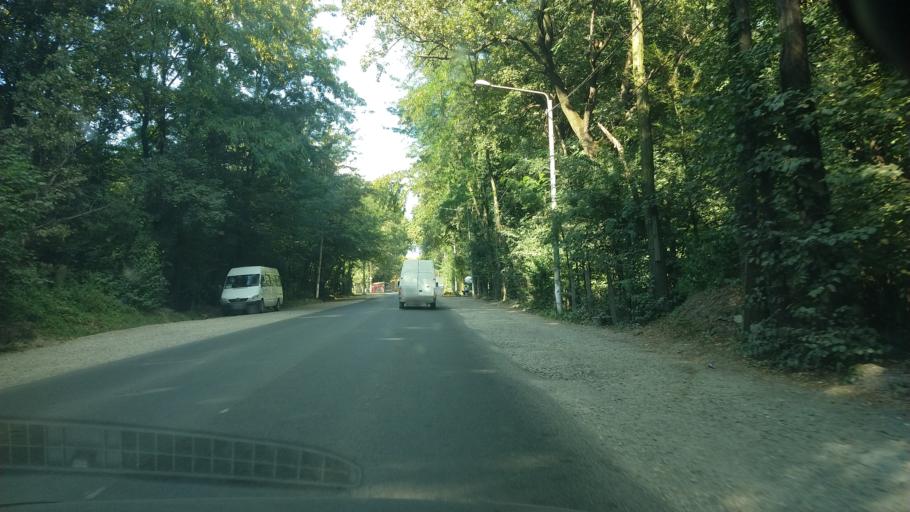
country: RO
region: Ilfov
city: Stefanestii de Jos
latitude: 44.5162
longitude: 26.1911
